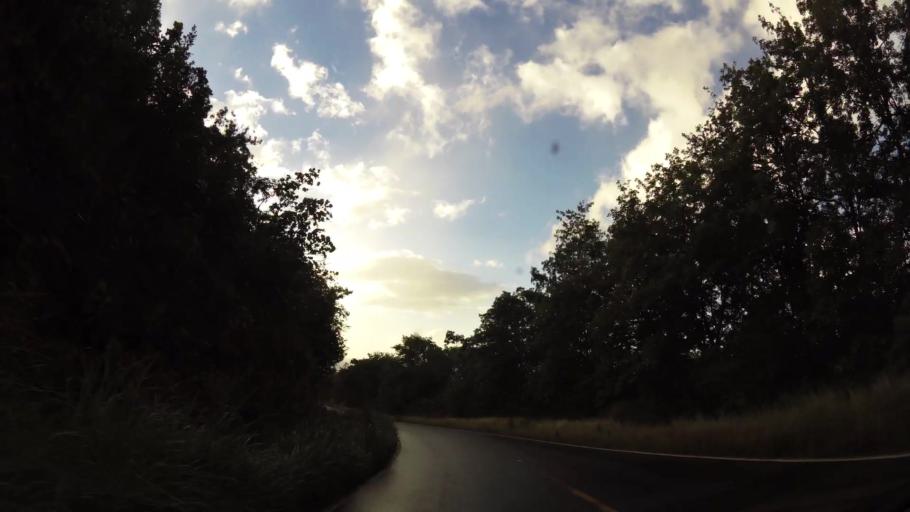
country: DM
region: Saint Peter
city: Colihaut
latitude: 15.5299
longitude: -61.4677
